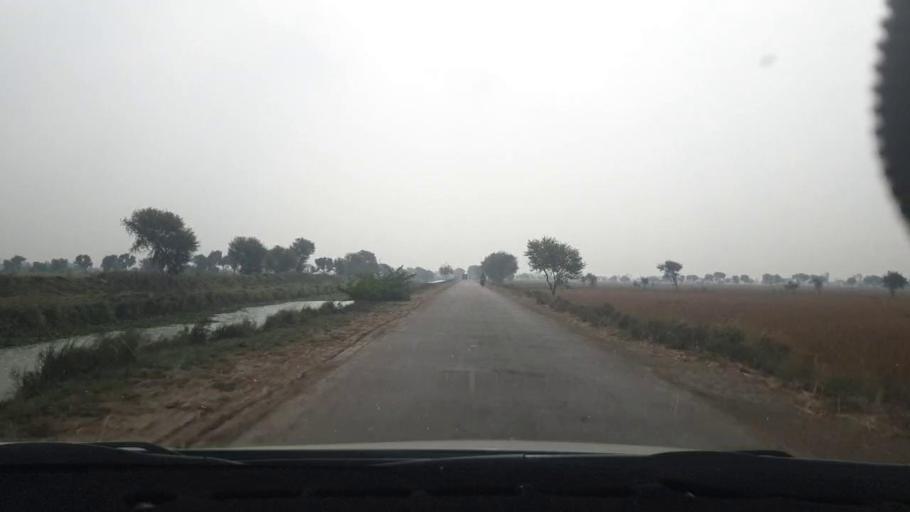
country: PK
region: Sindh
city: Tando Muhammad Khan
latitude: 25.0696
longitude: 68.5382
